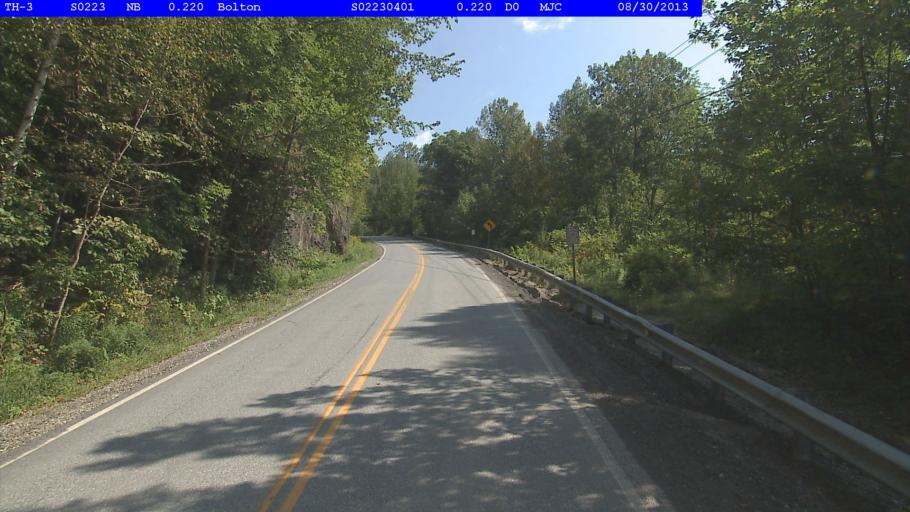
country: US
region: Vermont
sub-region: Washington County
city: Waterbury
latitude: 44.3754
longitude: -72.8764
